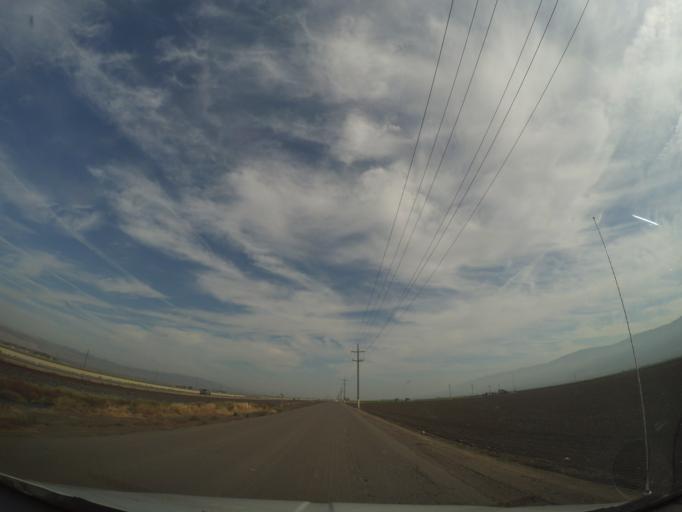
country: US
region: California
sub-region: Monterey County
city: Chualar
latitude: 36.5450
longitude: -121.4926
